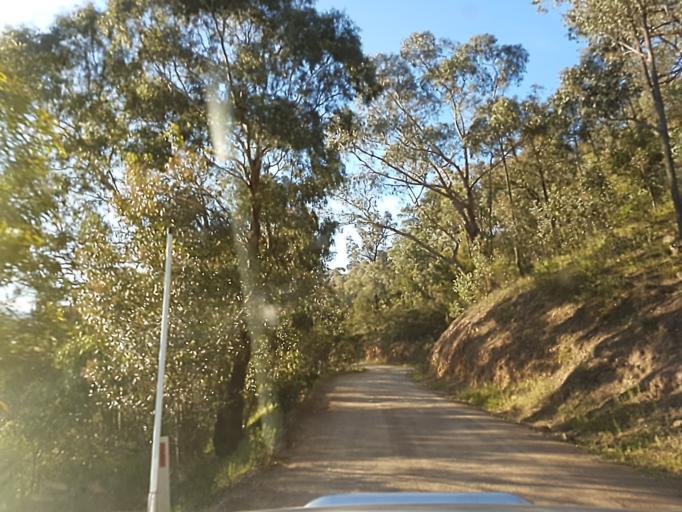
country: AU
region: Victoria
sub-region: East Gippsland
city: Bairnsdale
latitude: -37.4141
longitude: 147.1247
